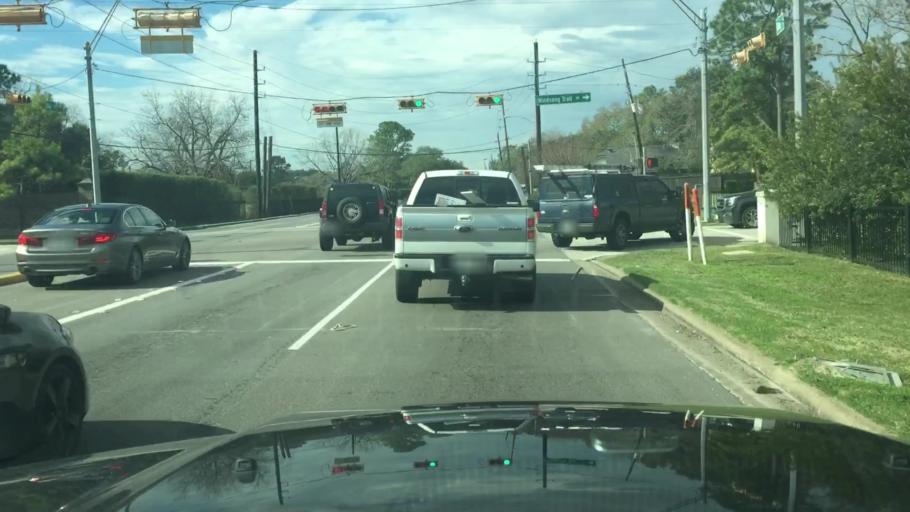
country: US
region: Texas
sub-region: Harris County
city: Oak Cliff Place
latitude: 29.8312
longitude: -95.6748
